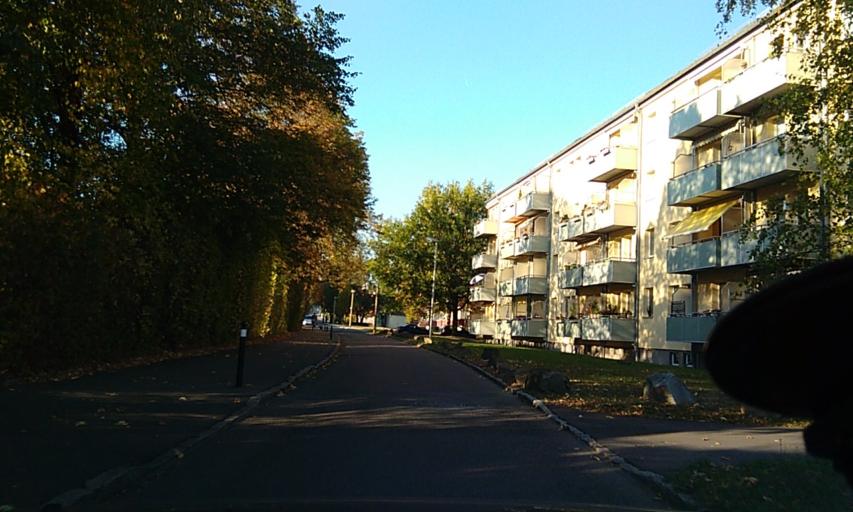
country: DE
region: Saxony
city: Wittgensdorf
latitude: 50.8399
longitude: 12.8709
